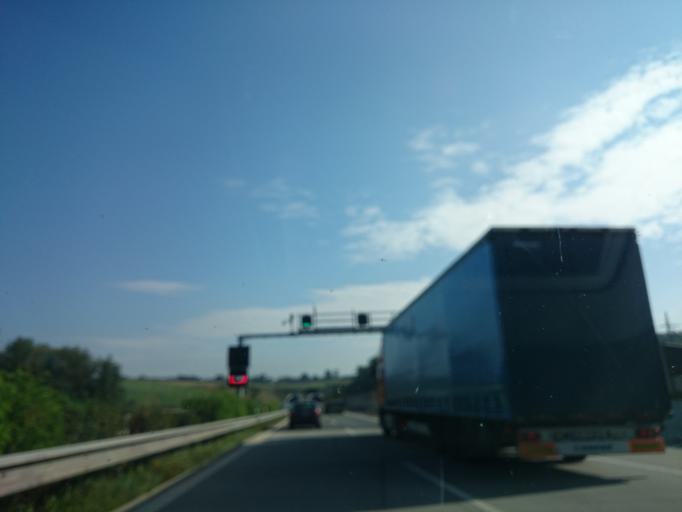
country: CZ
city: Klimkovice
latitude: 49.7865
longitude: 18.1072
